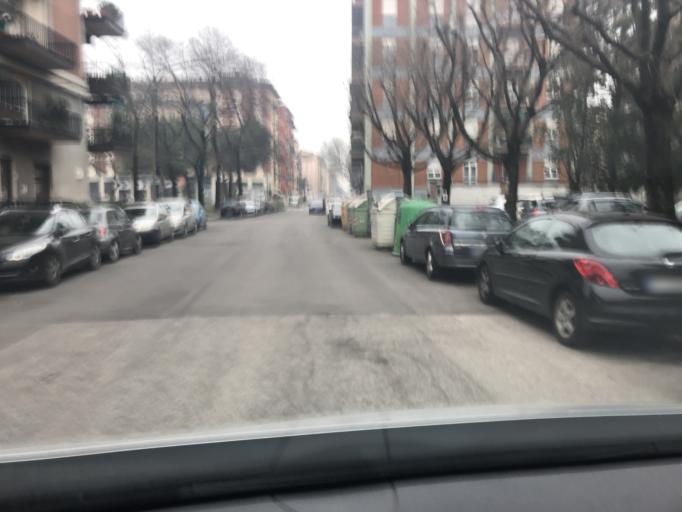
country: IT
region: Veneto
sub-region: Provincia di Verona
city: Verona
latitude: 45.4211
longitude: 10.9567
